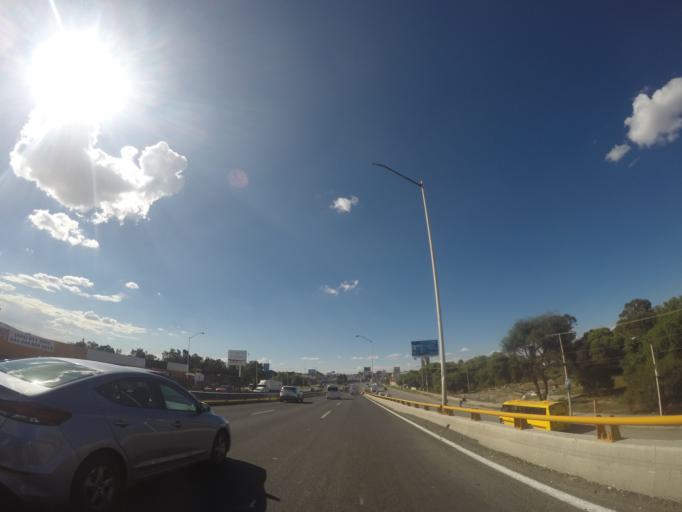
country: MX
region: San Luis Potosi
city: La Pila
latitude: 22.0842
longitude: -100.8784
